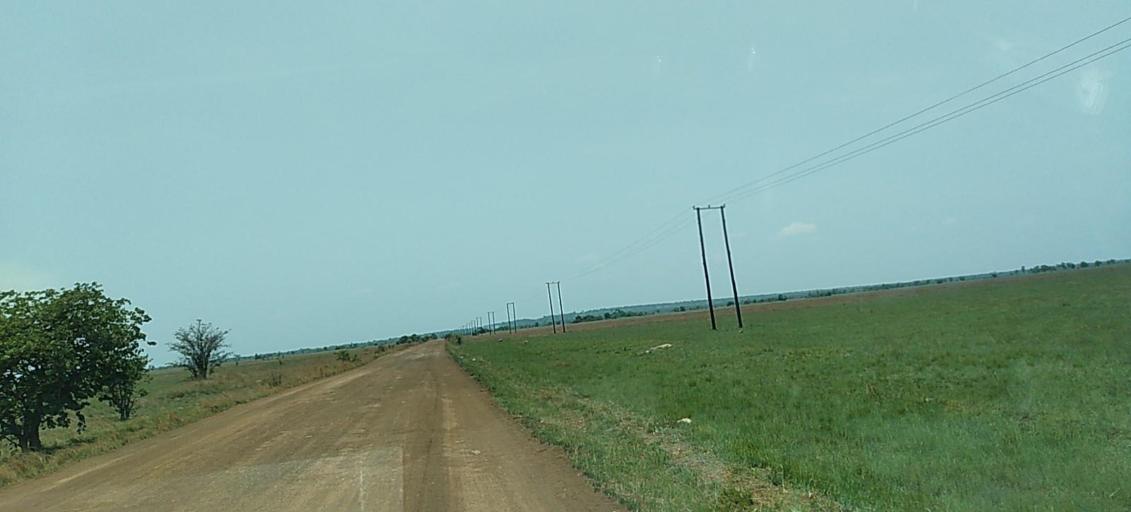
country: ZM
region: Copperbelt
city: Mpongwe
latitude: -13.6646
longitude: 27.8522
